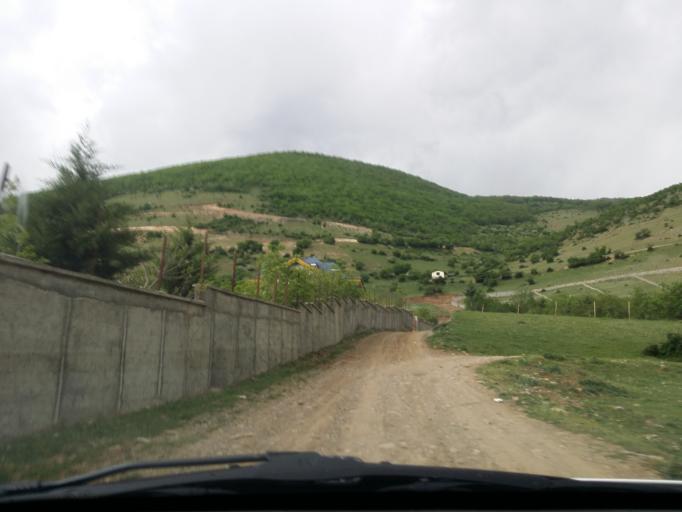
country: IR
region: Mazandaran
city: `Abbasabad
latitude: 36.5076
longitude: 51.1396
